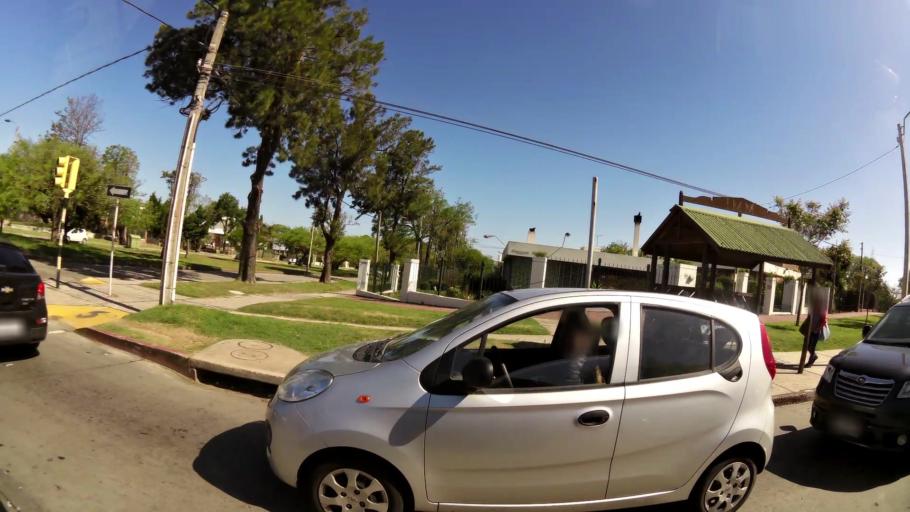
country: UY
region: Canelones
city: Paso de Carrasco
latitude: -34.8914
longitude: -56.0734
